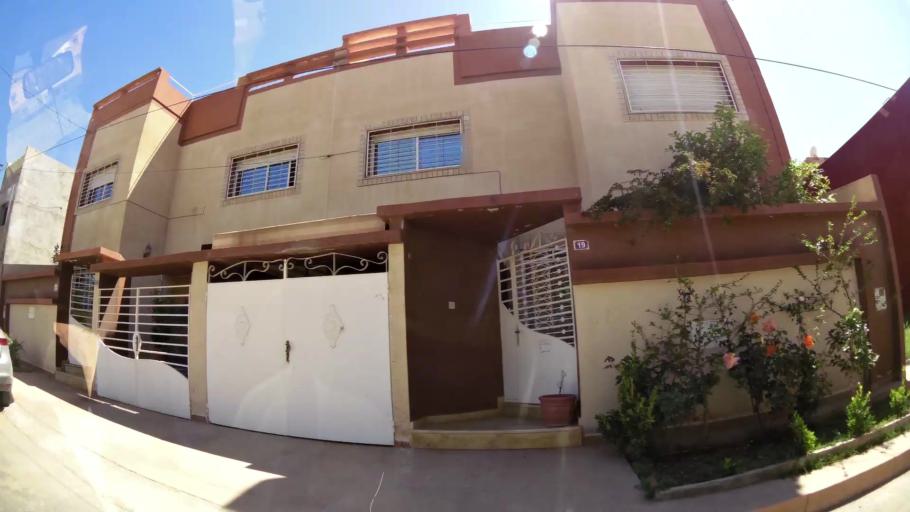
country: MA
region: Oriental
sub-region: Oujda-Angad
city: Oujda
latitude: 34.6484
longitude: -1.9107
